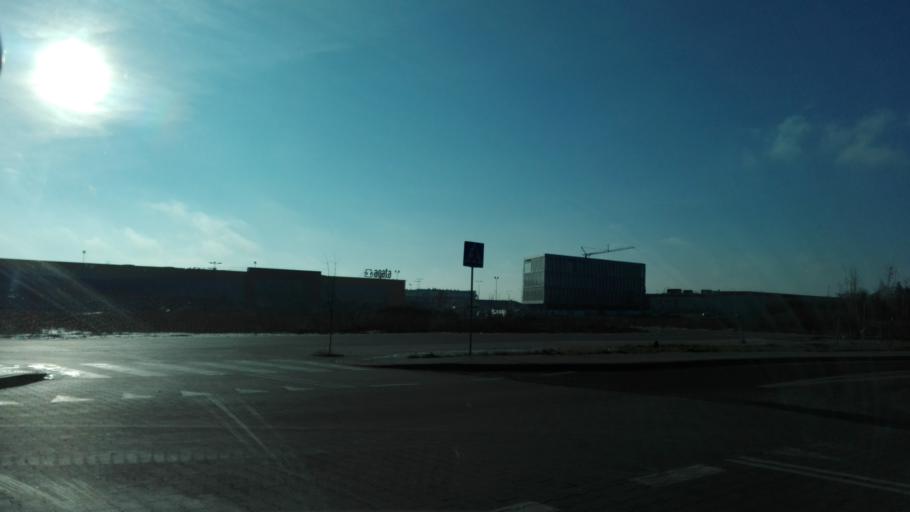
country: PL
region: Lublin Voivodeship
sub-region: Powiat lubelski
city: Kozubszczyzna
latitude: 51.2299
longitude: 22.4828
